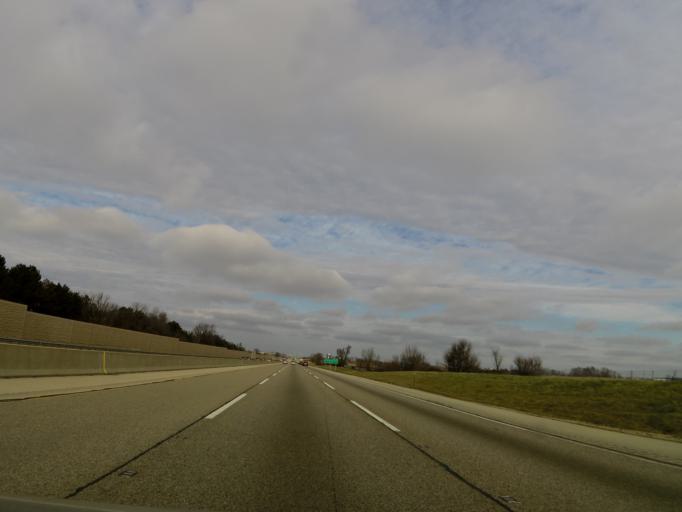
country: US
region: Illinois
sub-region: Winnebago County
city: Cherry Valley
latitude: 42.3046
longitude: -88.9646
